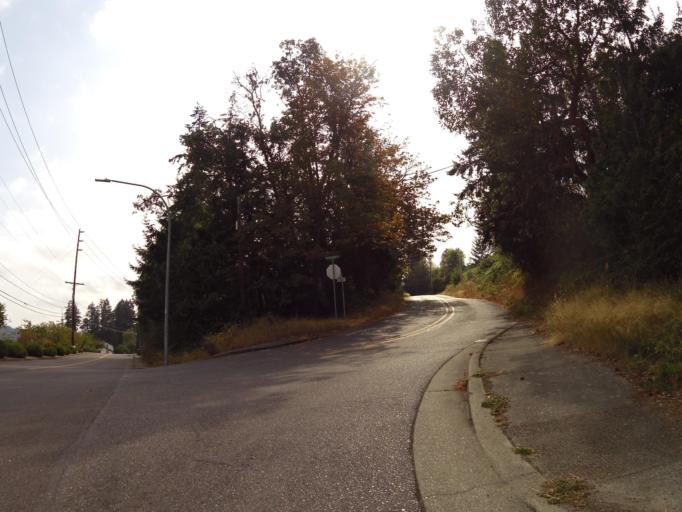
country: US
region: Washington
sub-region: Kitsap County
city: Navy Yard City
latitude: 47.5541
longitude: -122.6735
